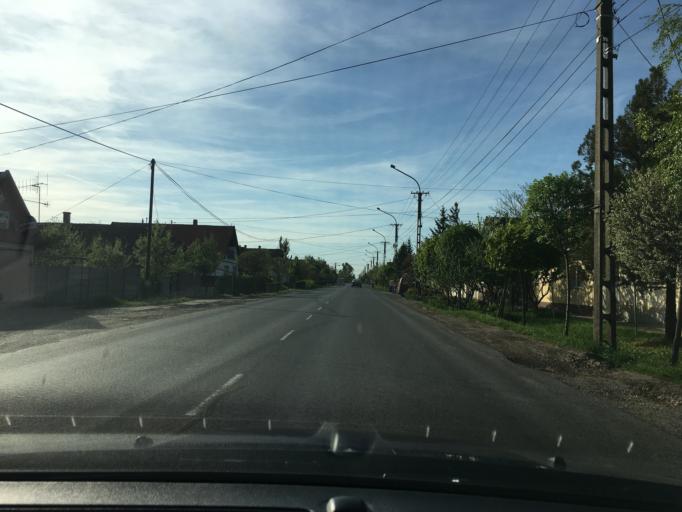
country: HU
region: Bekes
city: Korostarcsa
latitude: 46.8731
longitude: 21.0227
